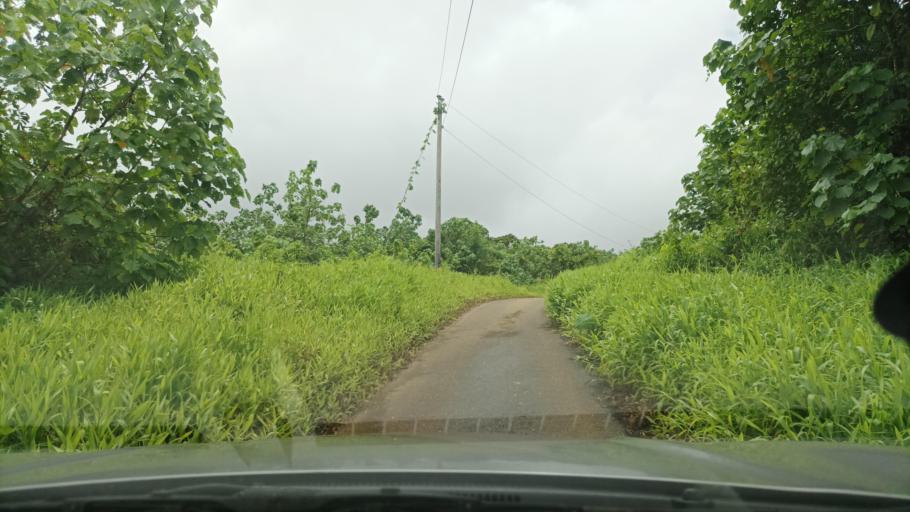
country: FM
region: Pohnpei
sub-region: Madolenihm Municipality
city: Madolenihm Municipality Government
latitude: 6.8929
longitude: 158.2898
